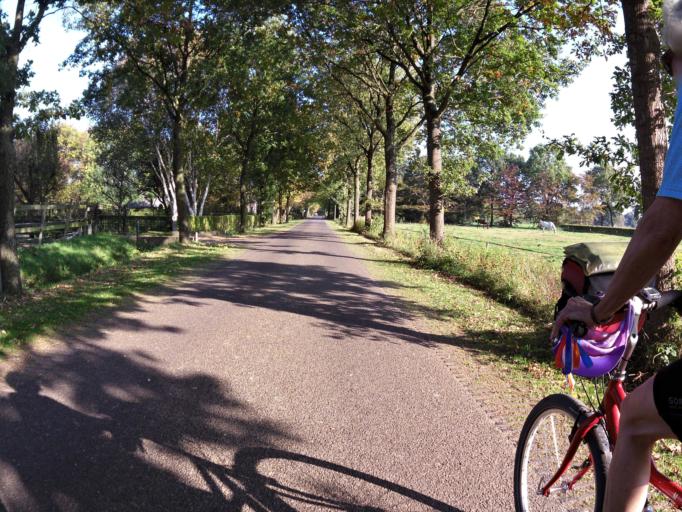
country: NL
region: North Brabant
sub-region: Gemeente Laarbeek
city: Aarle-Rixtel
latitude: 51.5446
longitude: 5.6831
